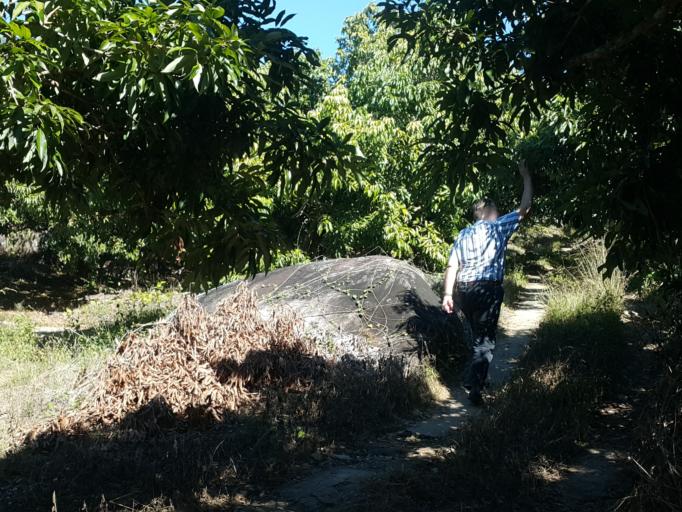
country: TH
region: Chiang Mai
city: Chiang Mai
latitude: 18.8027
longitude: 98.8672
